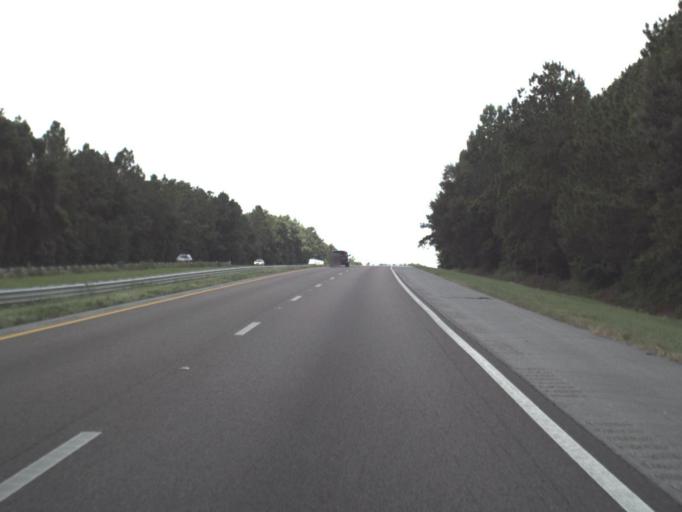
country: US
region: Florida
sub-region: Hernando County
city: Hill 'n Dale
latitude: 28.4752
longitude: -82.2582
